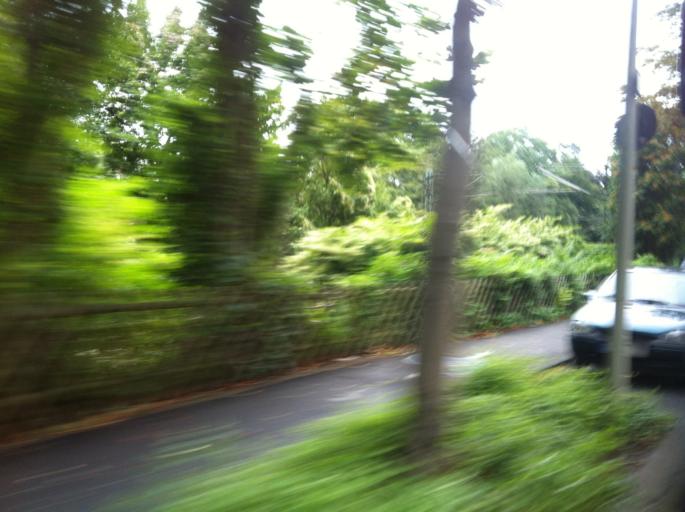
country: DE
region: North Rhine-Westphalia
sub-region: Regierungsbezirk Koln
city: Bonn
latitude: 50.7276
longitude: 7.1051
